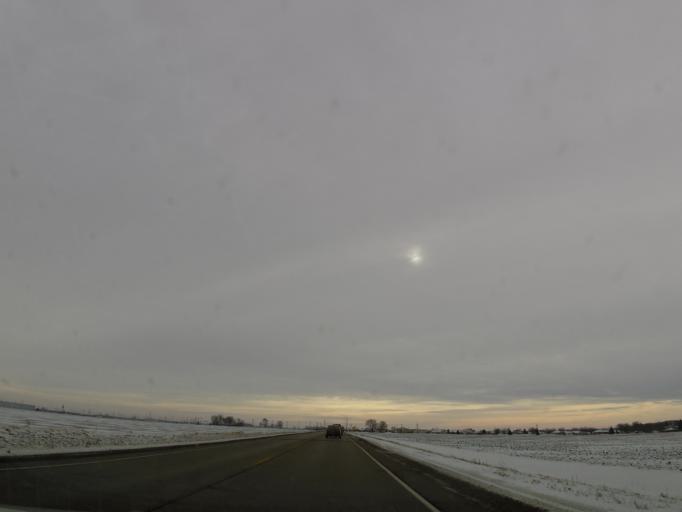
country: US
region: Illinois
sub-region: LaSalle County
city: Peru
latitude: 41.3002
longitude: -89.1060
